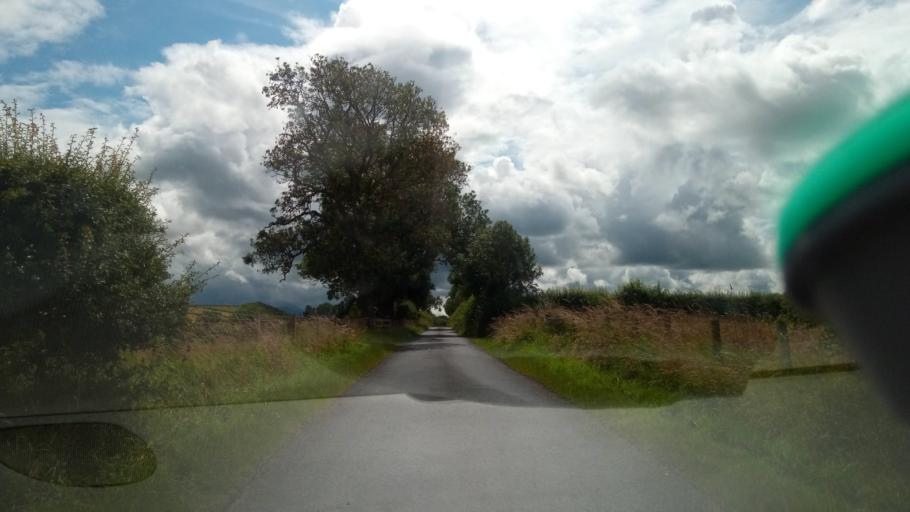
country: GB
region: Scotland
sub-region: The Scottish Borders
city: Kelso
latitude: 55.5101
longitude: -2.4200
